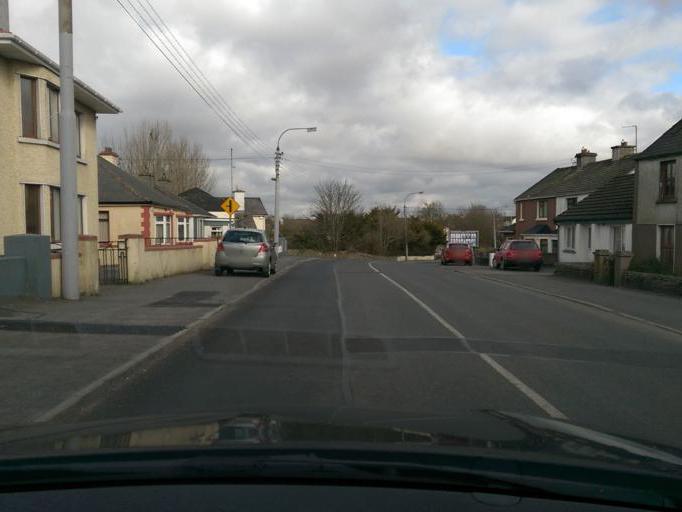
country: IE
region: Leinster
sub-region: An Iarmhi
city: Athlone
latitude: 53.4247
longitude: -7.9654
